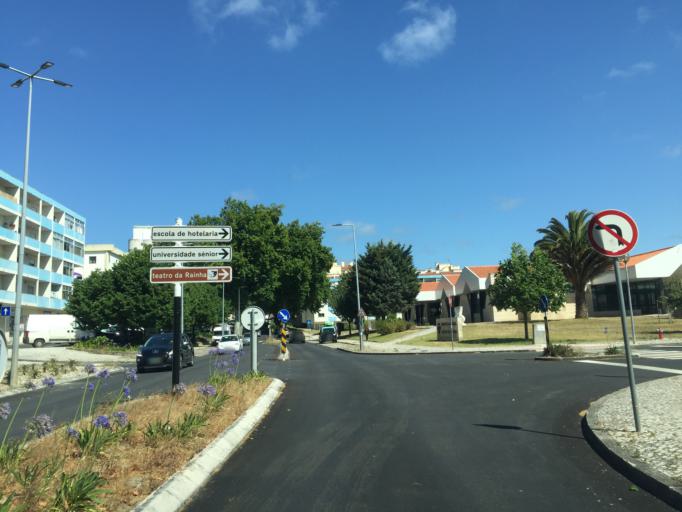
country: PT
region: Leiria
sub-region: Caldas da Rainha
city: Caldas da Rainha
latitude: 39.4030
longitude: -9.1427
